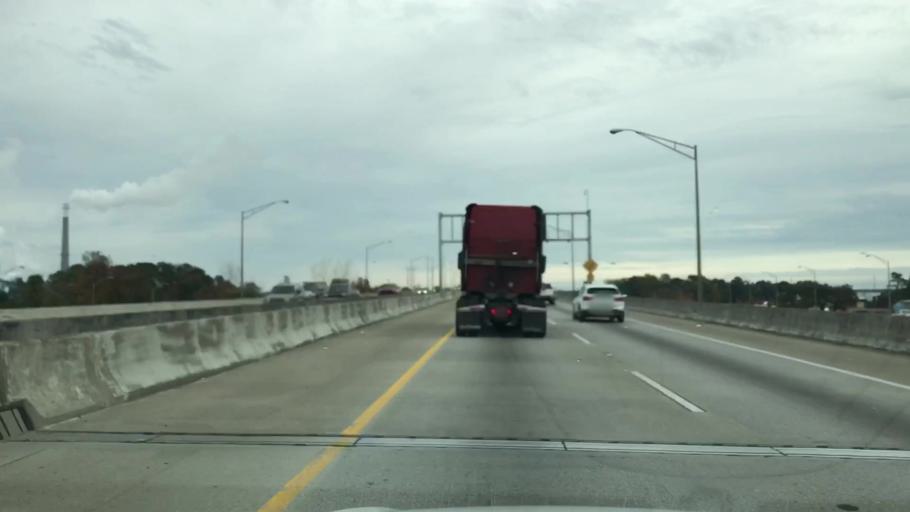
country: US
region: South Carolina
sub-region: Charleston County
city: North Charleston
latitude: 32.8933
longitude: -79.9788
